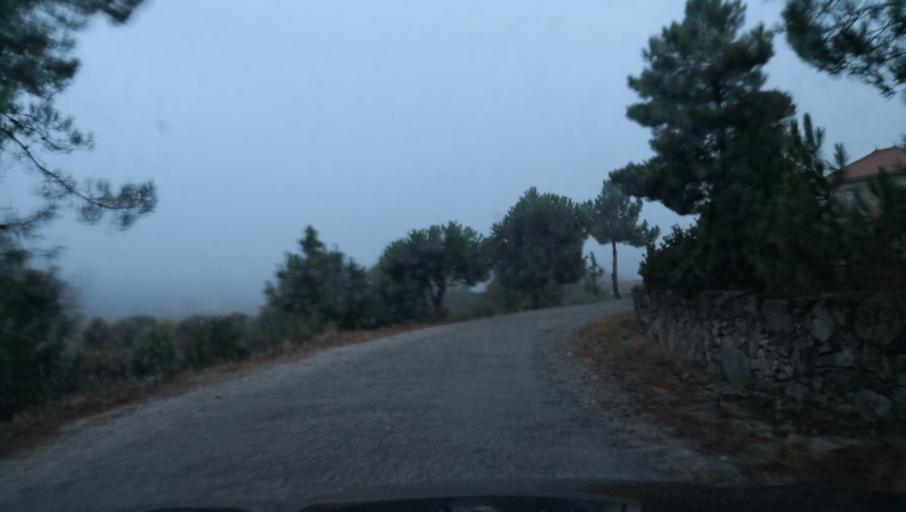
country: PT
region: Vila Real
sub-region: Sabrosa
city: Sabrosa
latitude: 41.2821
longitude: -7.5924
